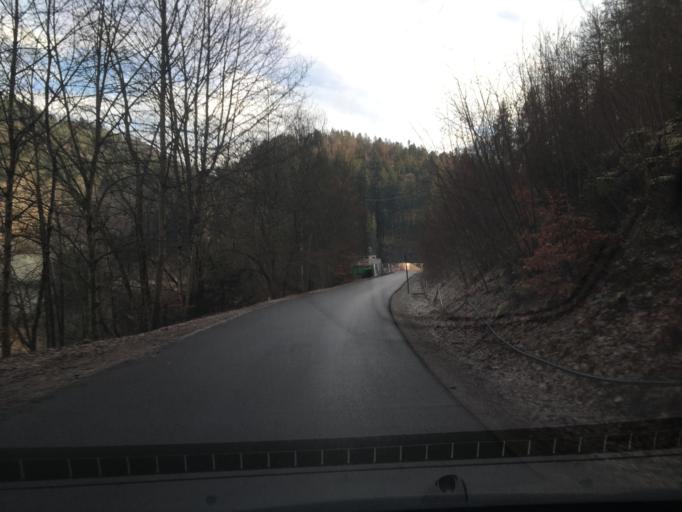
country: DE
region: Baden-Wuerttemberg
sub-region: Freiburg Region
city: Hausern
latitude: 47.7531
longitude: 8.1888
